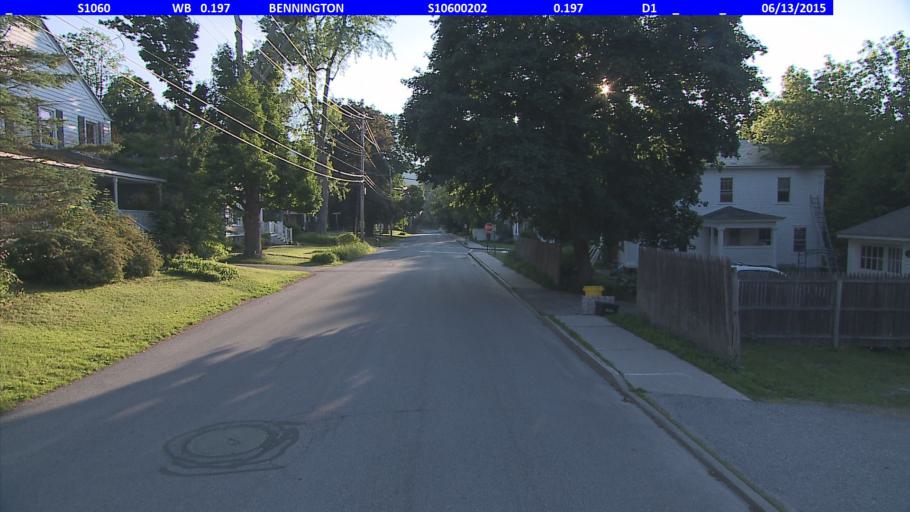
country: US
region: Vermont
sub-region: Bennington County
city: Bennington
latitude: 42.8746
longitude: -73.2002
